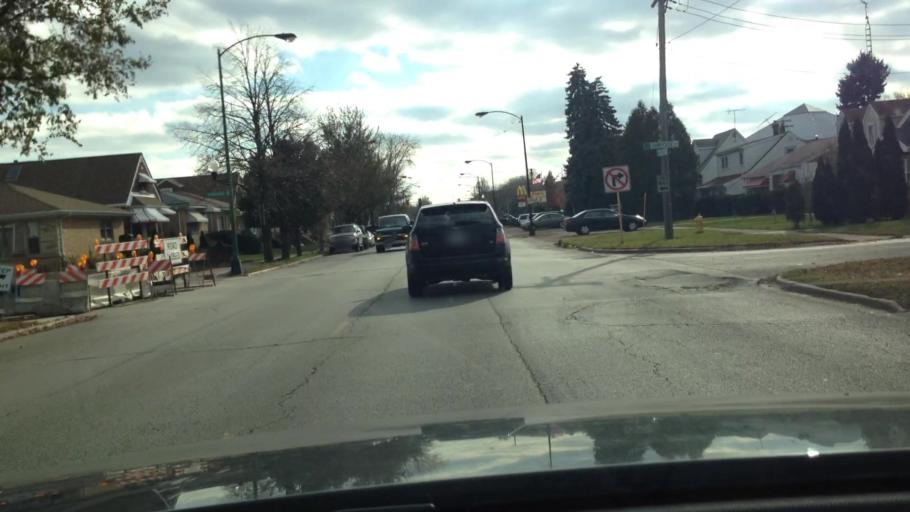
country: US
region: Illinois
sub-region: Cook County
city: Harwood Heights
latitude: 41.9623
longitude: -87.7869
